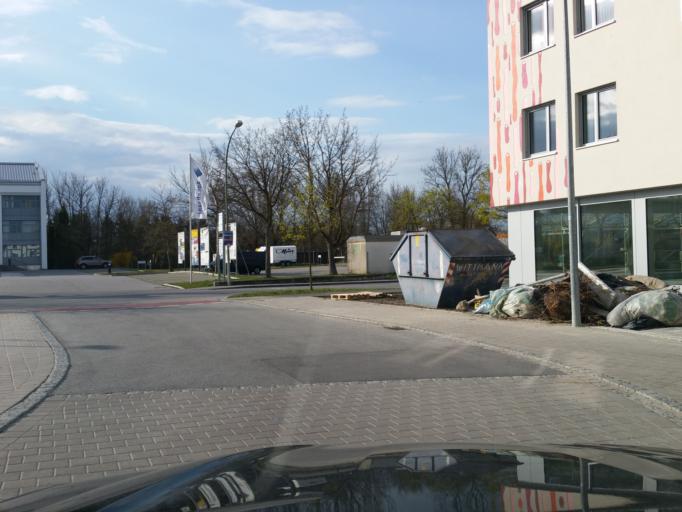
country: DE
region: Bavaria
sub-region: Lower Bavaria
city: Landshut
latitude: 48.5502
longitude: 12.1614
